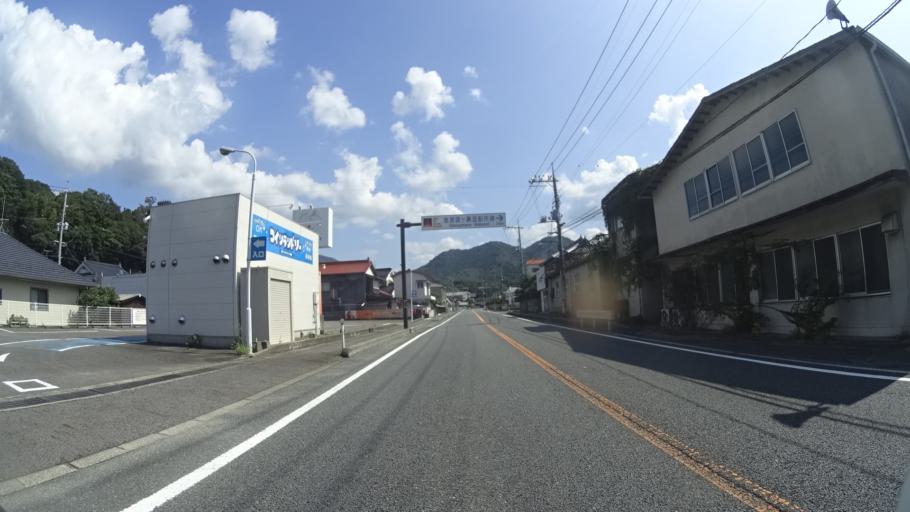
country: JP
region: Yamaguchi
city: Hagi
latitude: 34.4311
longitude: 131.4157
